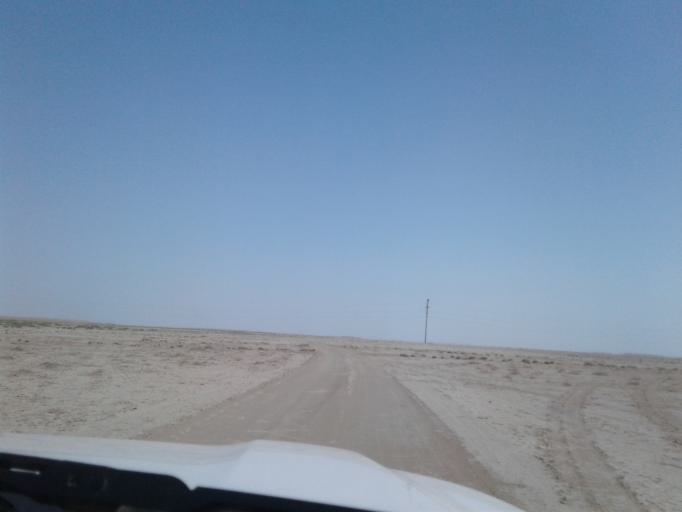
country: TM
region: Balkan
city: Gumdag
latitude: 38.3906
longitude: 54.4008
